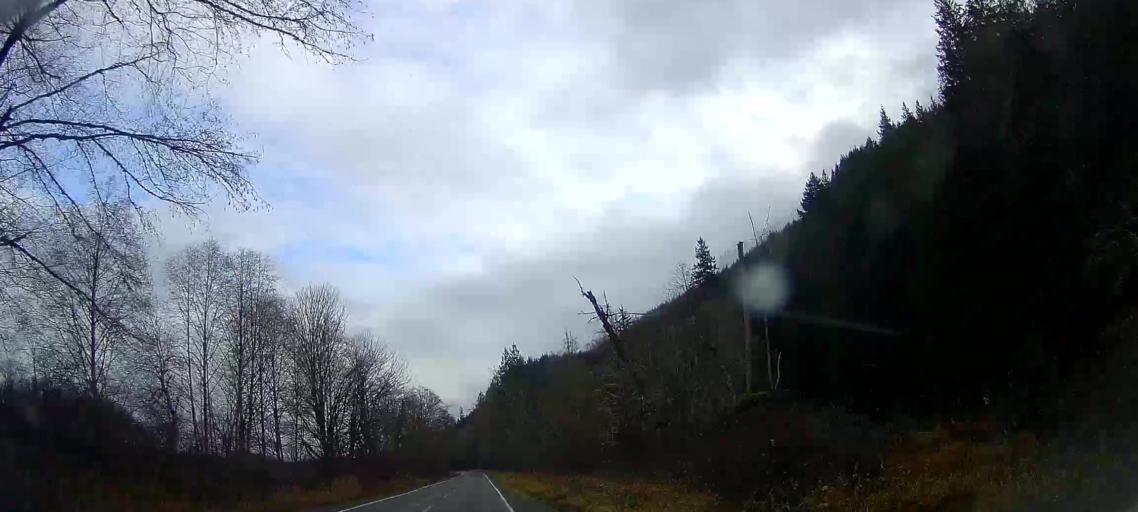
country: US
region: Washington
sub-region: Skagit County
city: Sedro-Woolley
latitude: 48.5161
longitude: -121.9600
